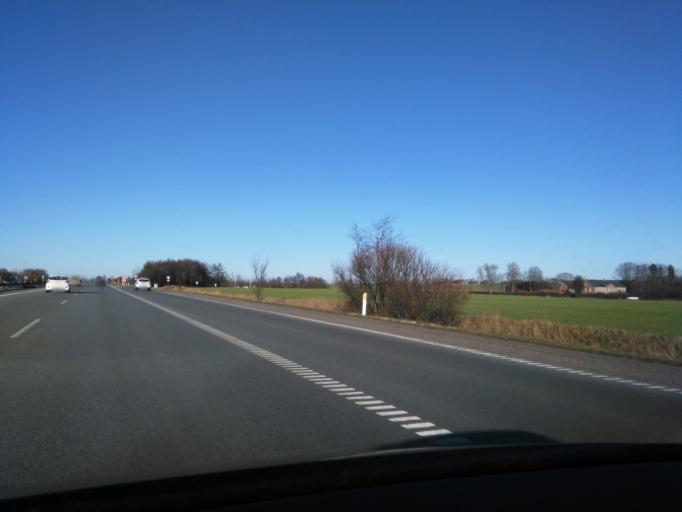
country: DK
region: Central Jutland
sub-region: Randers Kommune
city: Randers
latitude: 56.4877
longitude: 9.9806
